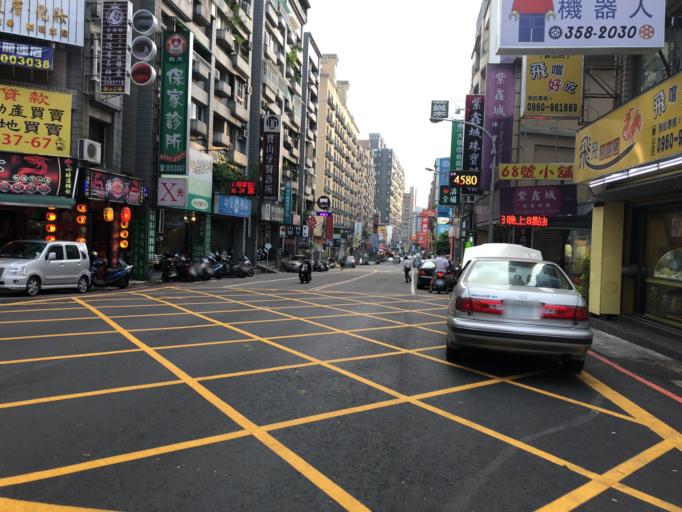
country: TW
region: Taiwan
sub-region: Taoyuan
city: Taoyuan
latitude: 25.0129
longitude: 121.3179
